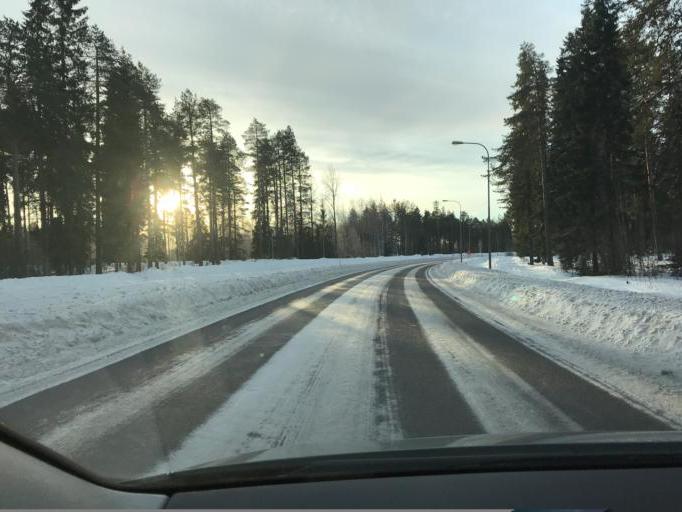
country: SE
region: Norrbotten
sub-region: Lulea Kommun
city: Gammelstad
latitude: 65.6316
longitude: 22.0360
